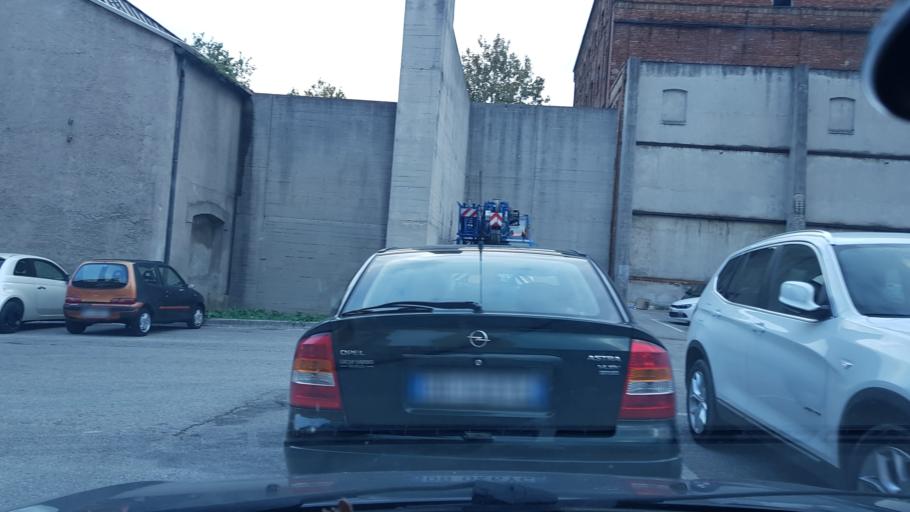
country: IT
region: Friuli Venezia Giulia
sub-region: Provincia di Trieste
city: Trieste
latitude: 45.6214
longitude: 13.7889
